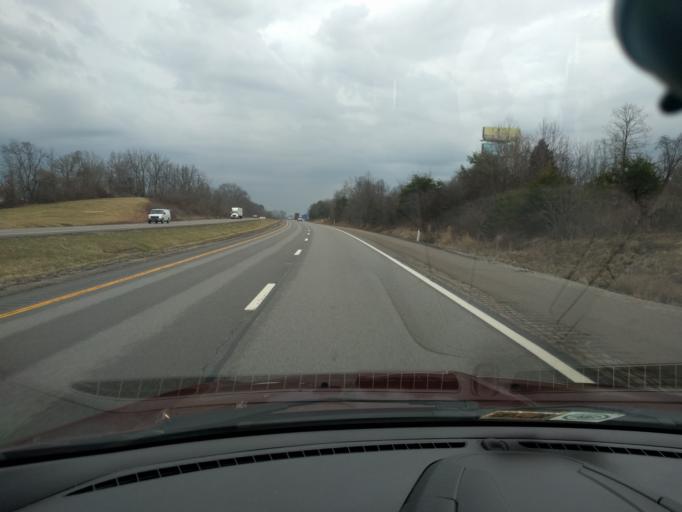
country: US
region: West Virginia
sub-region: Wood County
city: Williamstown
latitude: 39.3715
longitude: -81.4389
